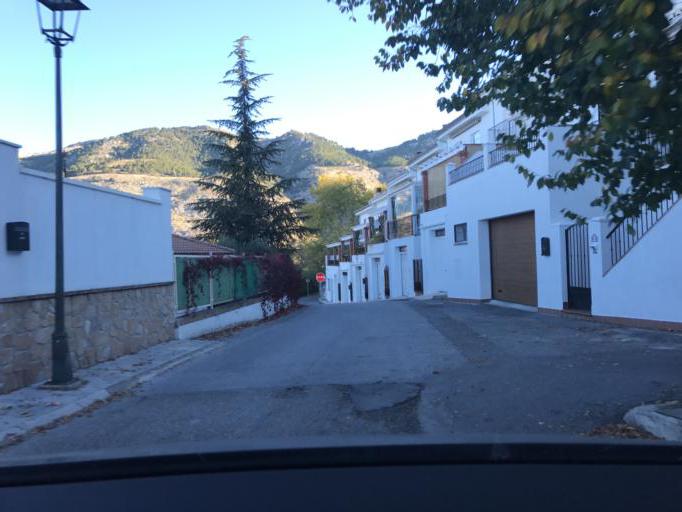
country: ES
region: Andalusia
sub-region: Provincia de Granada
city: Viznar
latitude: 37.2346
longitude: -3.5516
